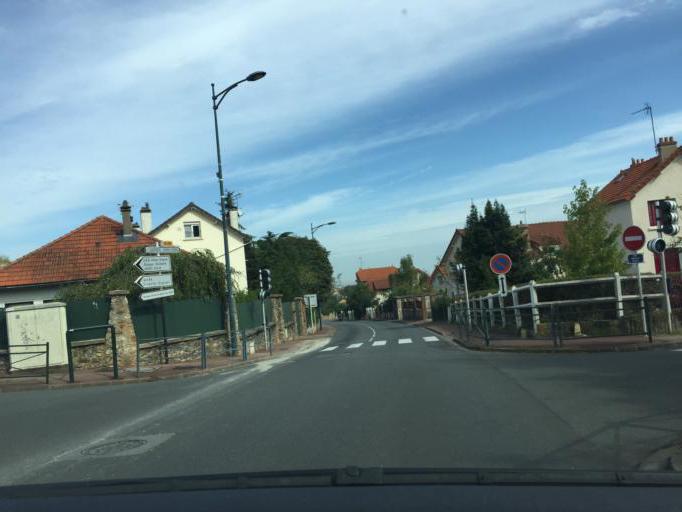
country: FR
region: Ile-de-France
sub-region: Departement de l'Essonne
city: Palaiseau
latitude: 48.7176
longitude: 2.2404
